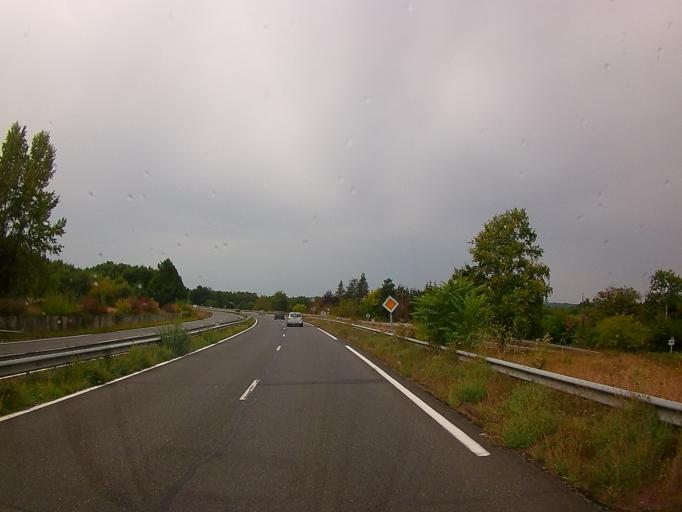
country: FR
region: Aquitaine
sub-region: Departement de la Dordogne
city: Neuvic
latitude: 45.0834
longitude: 0.4605
